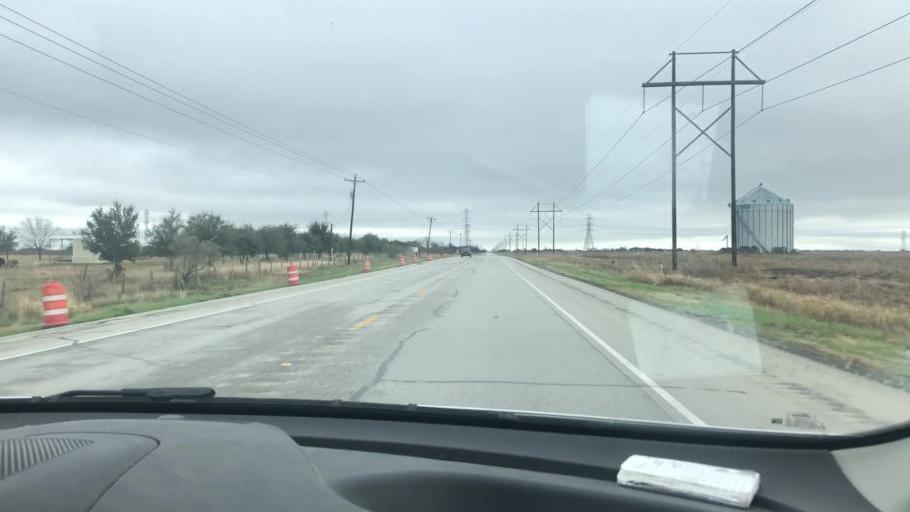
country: US
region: Texas
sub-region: Wharton County
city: Boling
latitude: 29.1791
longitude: -96.0073
